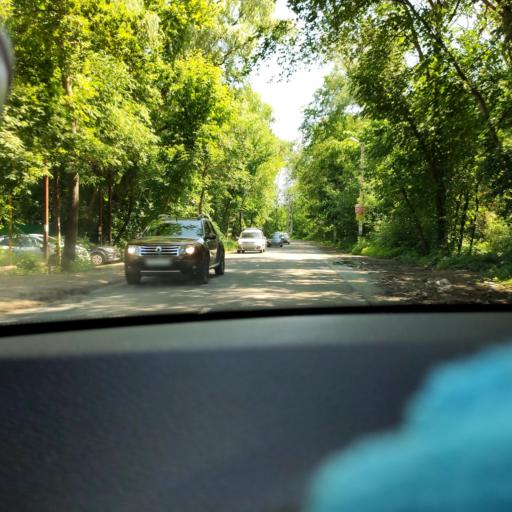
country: RU
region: Samara
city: Novokuybyshevsk
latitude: 53.1544
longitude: 49.9565
